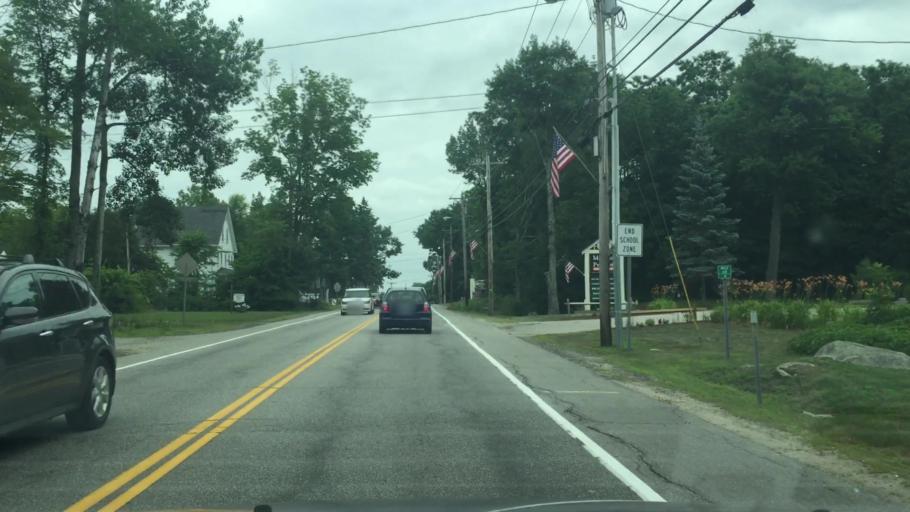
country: US
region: New Hampshire
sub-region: Carroll County
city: Moultonborough
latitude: 43.7516
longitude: -71.4000
